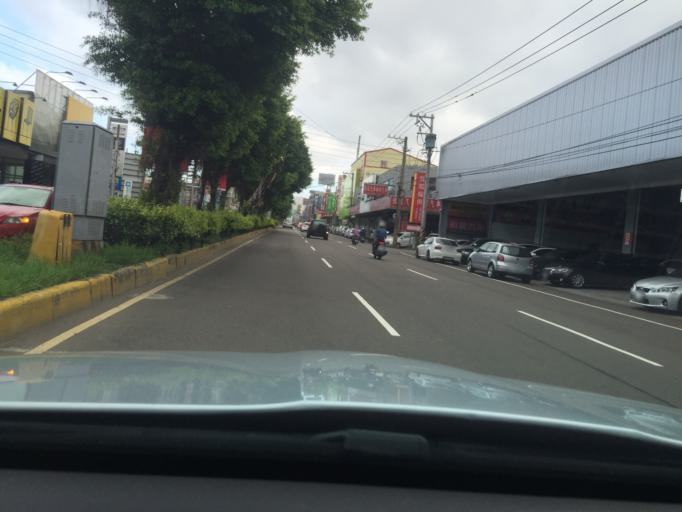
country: TW
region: Taiwan
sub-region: Hsinchu
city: Hsinchu
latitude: 24.8151
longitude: 120.9859
